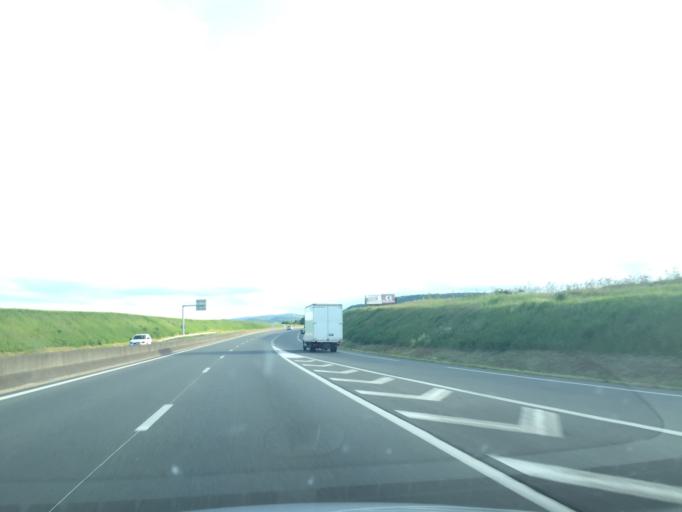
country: FR
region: Auvergne
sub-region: Departement du Puy-de-Dome
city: Menetrol
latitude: 45.8876
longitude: 3.1372
